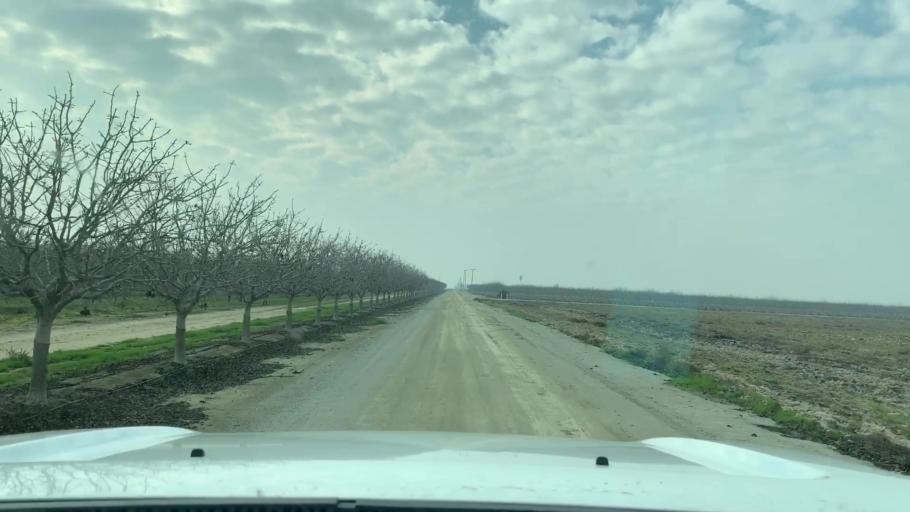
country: US
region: California
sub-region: Tulare County
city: Earlimart
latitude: 35.8337
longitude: -119.3647
